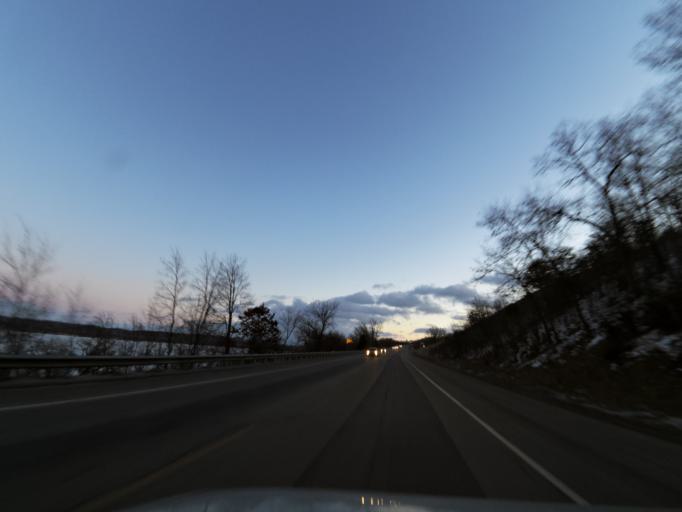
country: US
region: Wisconsin
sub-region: Saint Croix County
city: North Hudson
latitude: 44.9973
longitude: -92.7781
